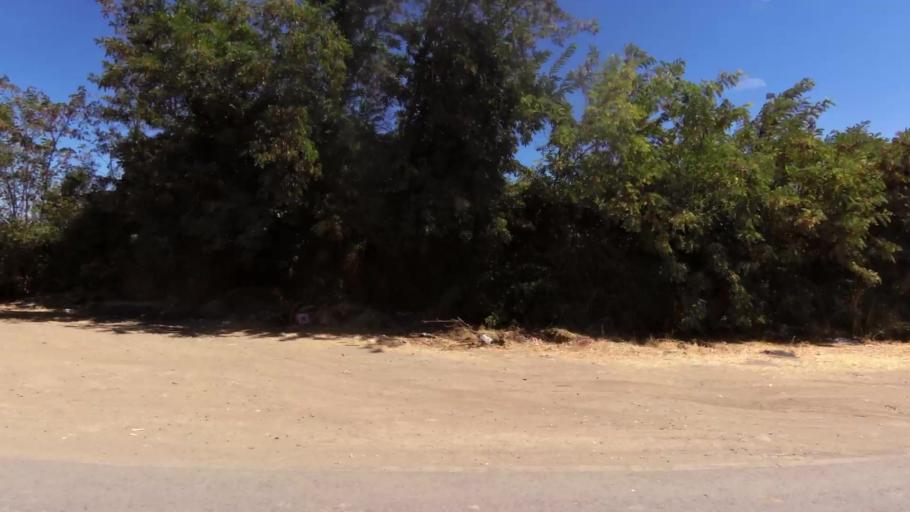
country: CL
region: O'Higgins
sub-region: Provincia de Cachapoal
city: Rancagua
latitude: -34.1605
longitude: -70.7000
